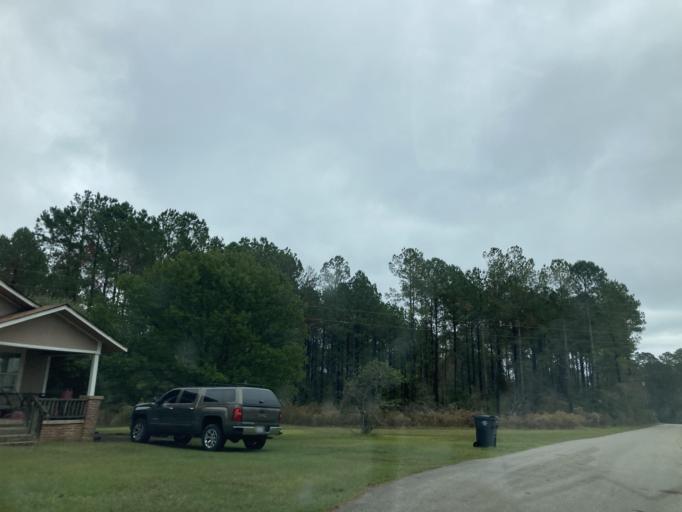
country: US
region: Mississippi
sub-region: Lamar County
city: Purvis
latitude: 31.1894
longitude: -89.4270
